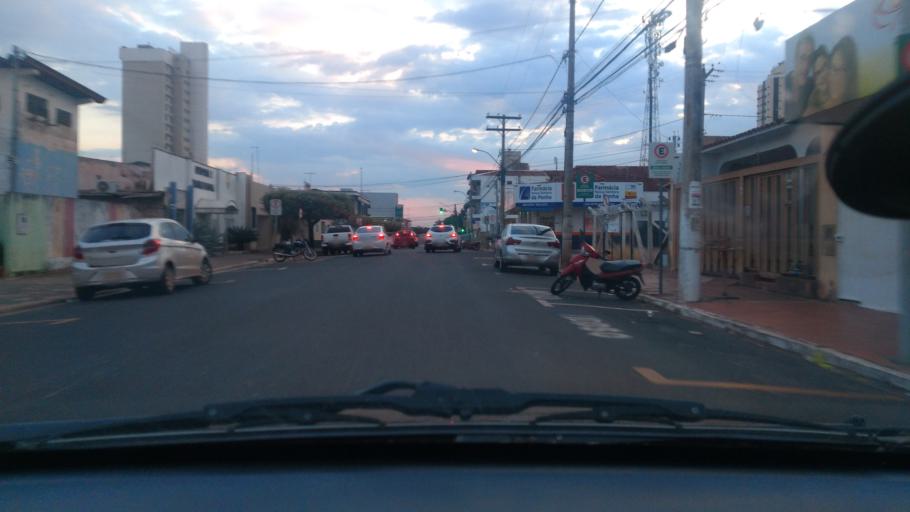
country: BR
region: Goias
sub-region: Santa Helena De Goias
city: Santa Helena de Goias
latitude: -17.7958
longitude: -50.9287
